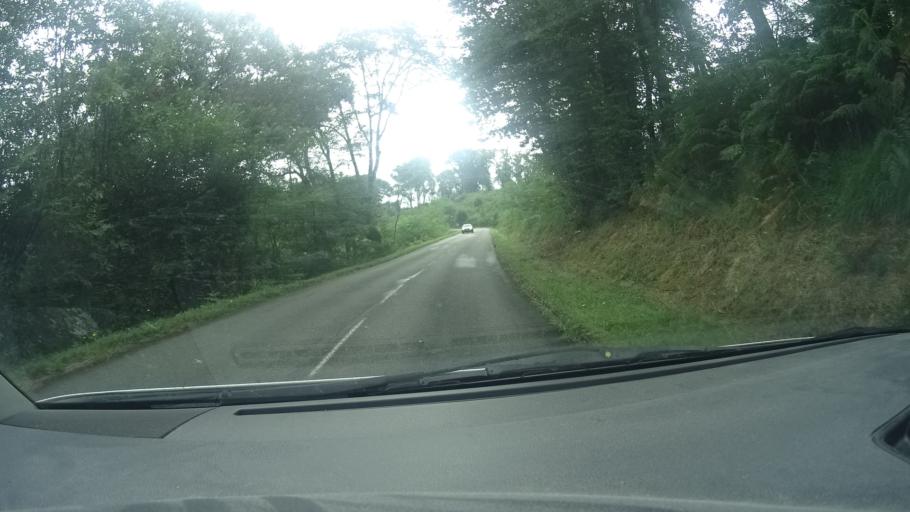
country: FR
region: Aquitaine
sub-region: Departement des Pyrenees-Atlantiques
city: Mont
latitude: 43.4881
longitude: -0.6883
